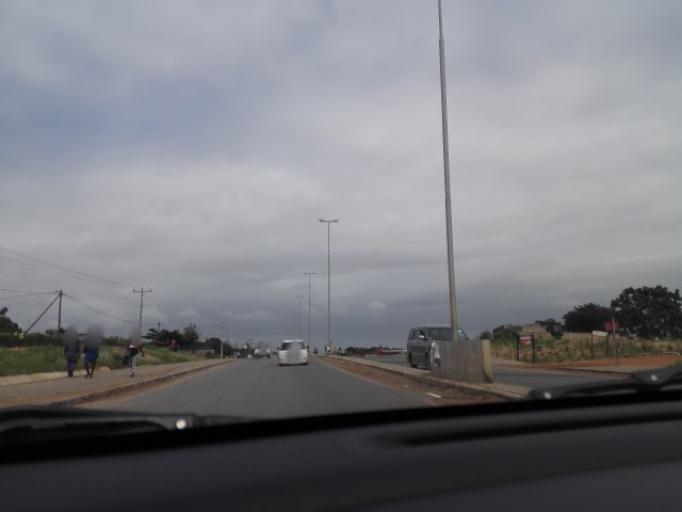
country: MZ
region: Maputo City
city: Maputo
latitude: -25.8261
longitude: 32.6009
